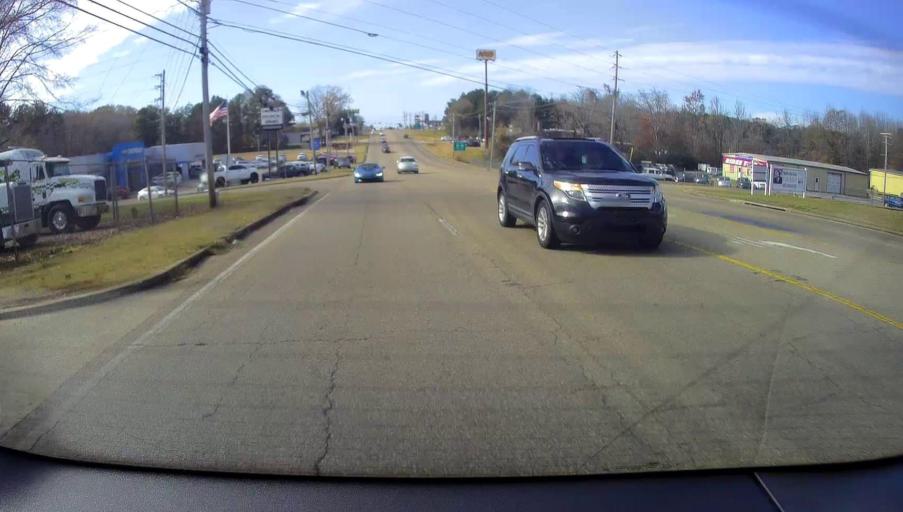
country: US
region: Mississippi
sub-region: Alcorn County
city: Corinth
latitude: 34.9308
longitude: -88.5403
